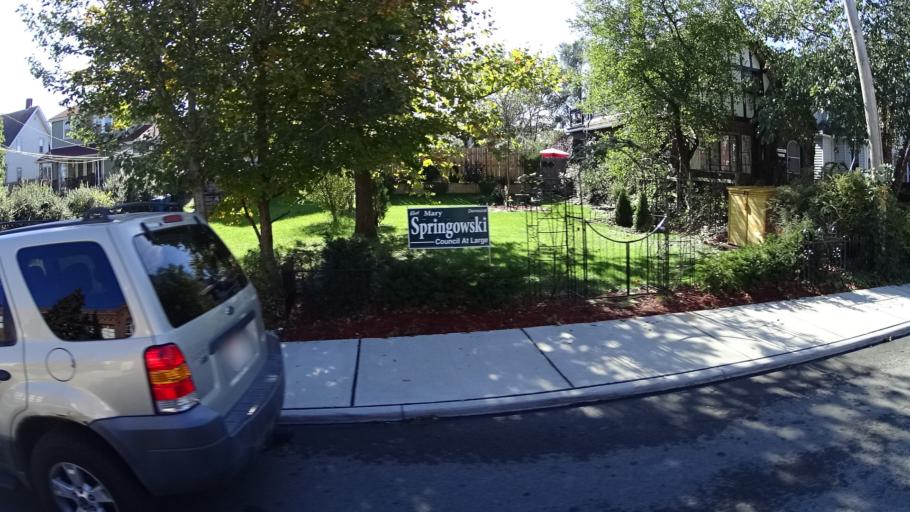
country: US
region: Ohio
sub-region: Lorain County
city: Lorain
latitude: 41.4660
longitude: -82.1835
